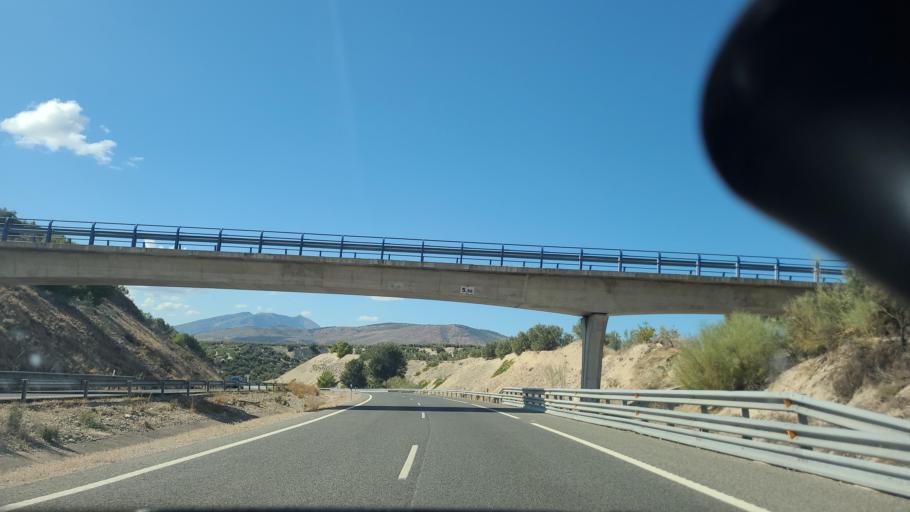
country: ES
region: Andalusia
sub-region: Provincia de Jaen
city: Pegalajar
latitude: 37.7188
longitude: -3.6513
